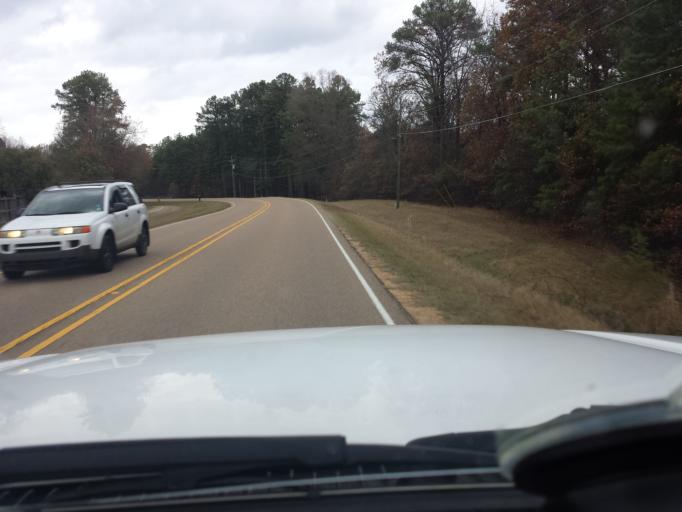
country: US
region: Mississippi
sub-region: Madison County
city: Madison
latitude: 32.4111
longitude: -90.0090
